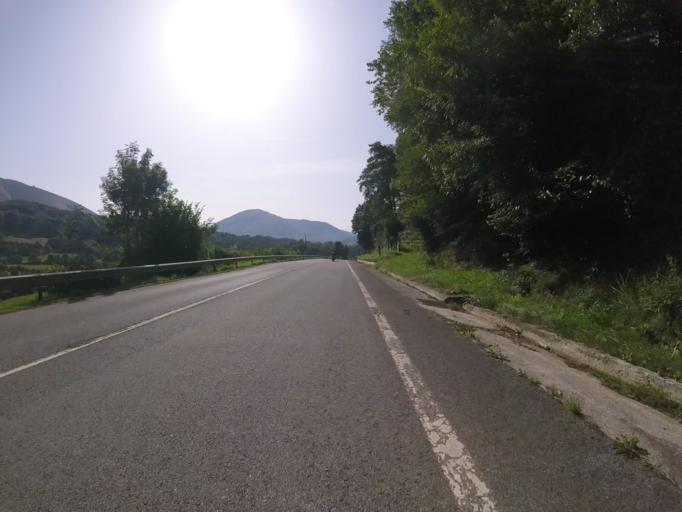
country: ES
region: Navarre
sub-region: Provincia de Navarra
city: Zugarramurdi
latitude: 43.1991
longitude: -1.4845
